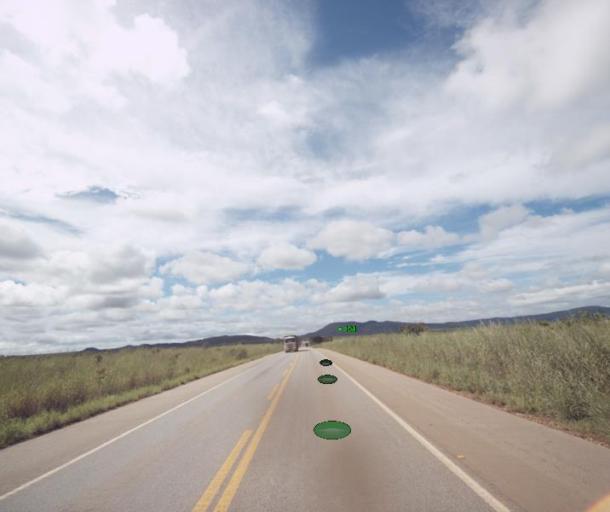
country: BR
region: Goias
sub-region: Barro Alto
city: Barro Alto
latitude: -15.1839
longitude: -48.7838
